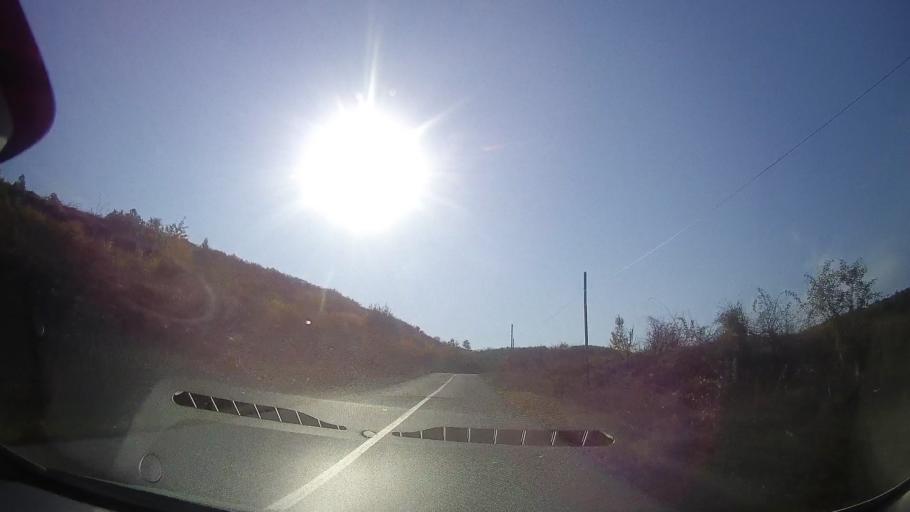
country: RO
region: Timis
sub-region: Oras Recas
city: Recas
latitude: 45.8416
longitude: 21.5211
